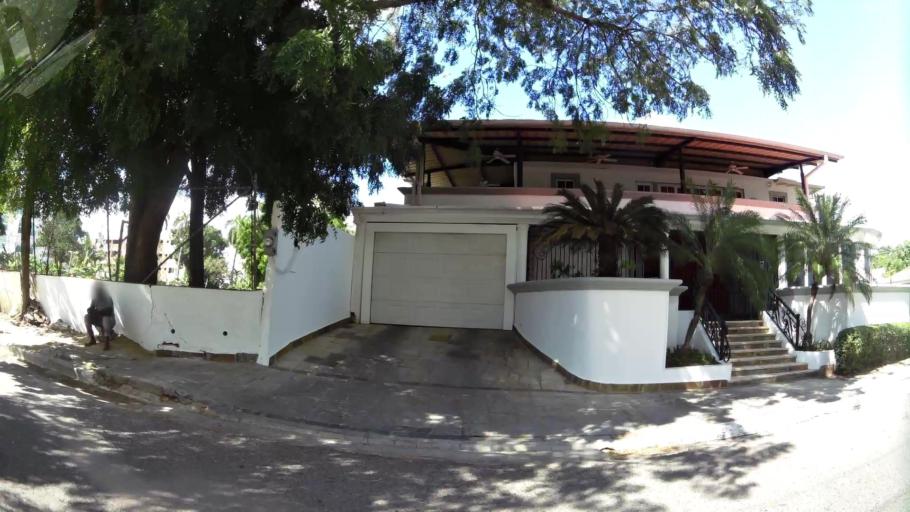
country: DO
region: Santiago
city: Santiago de los Caballeros
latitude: 19.4568
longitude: -70.6795
